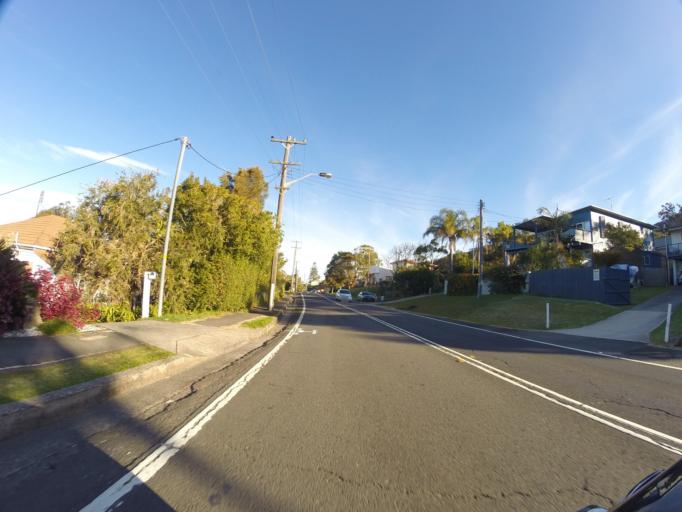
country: AU
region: New South Wales
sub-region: Wollongong
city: Bulli
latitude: -34.2779
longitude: 150.9542
